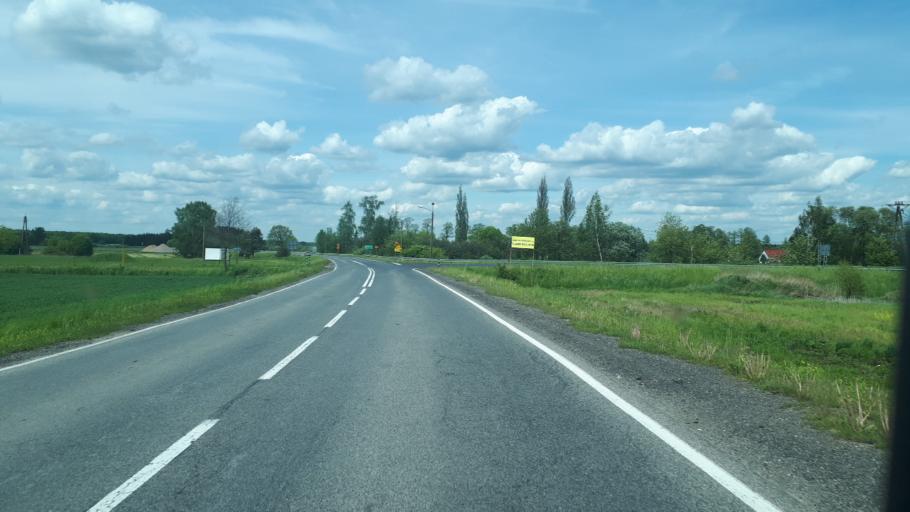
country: PL
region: Silesian Voivodeship
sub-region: Powiat gliwicki
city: Wielowies
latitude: 50.5252
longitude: 18.6054
